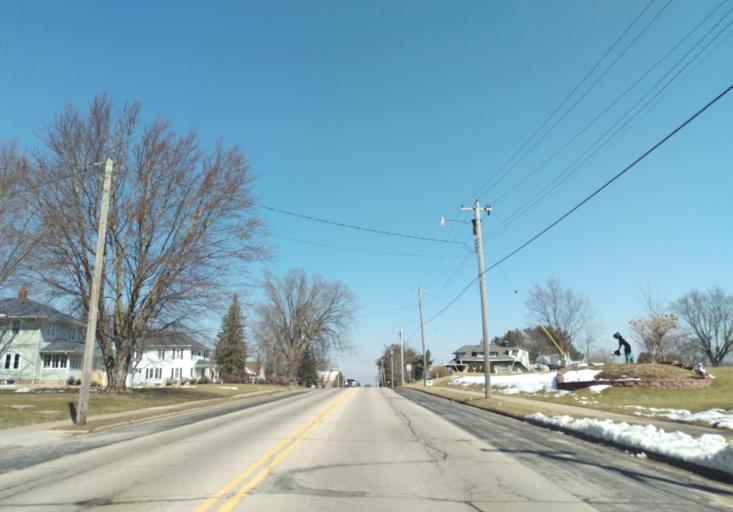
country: US
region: Wisconsin
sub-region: Vernon County
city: Westby
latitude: 43.6461
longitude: -90.8621
